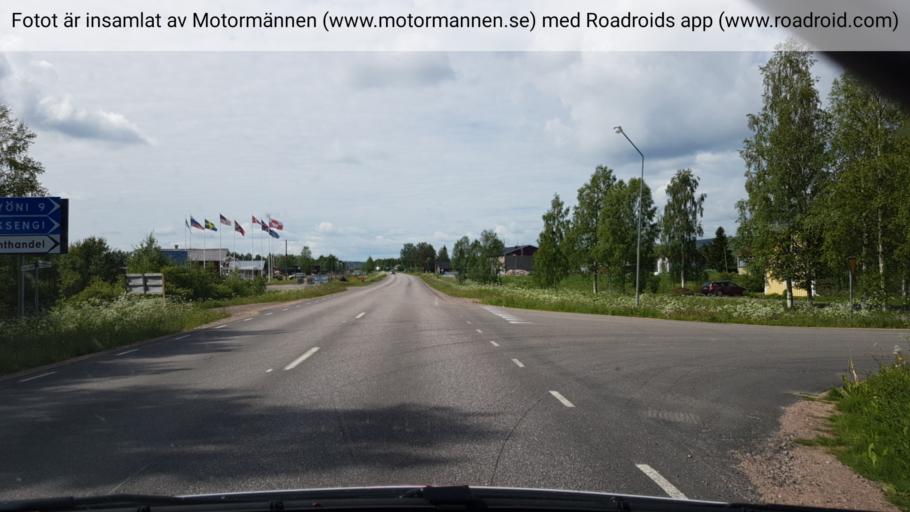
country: FI
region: Lapland
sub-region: Torniolaakso
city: Pello
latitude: 66.5613
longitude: 23.8387
